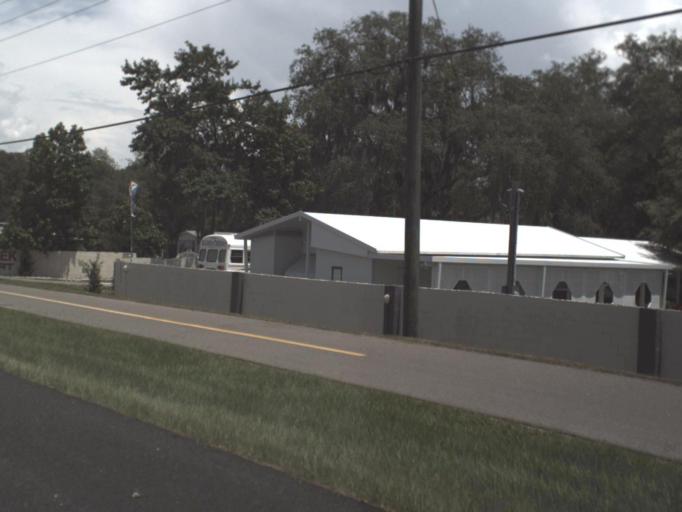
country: US
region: Florida
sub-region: Hillsborough County
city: Riverview
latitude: 27.8449
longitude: -82.3267
